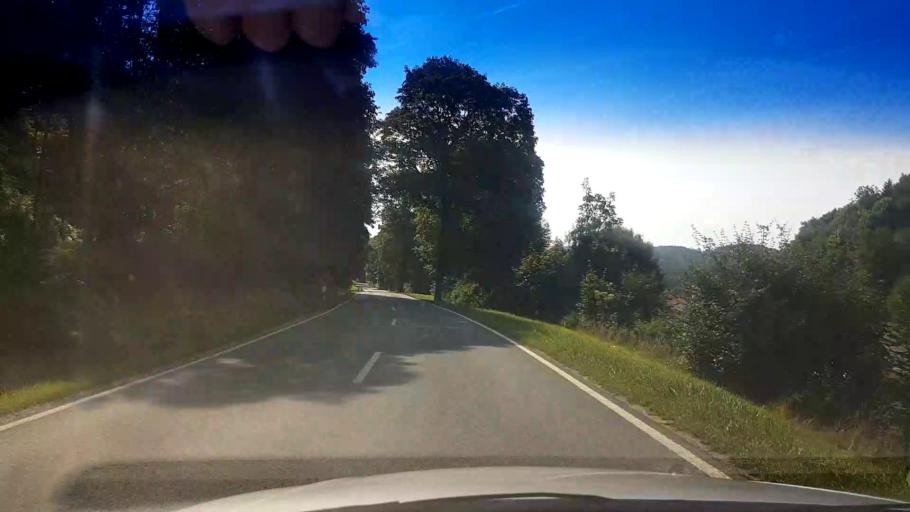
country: DE
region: Bavaria
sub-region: Upper Franconia
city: Hollfeld
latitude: 49.9400
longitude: 11.3396
